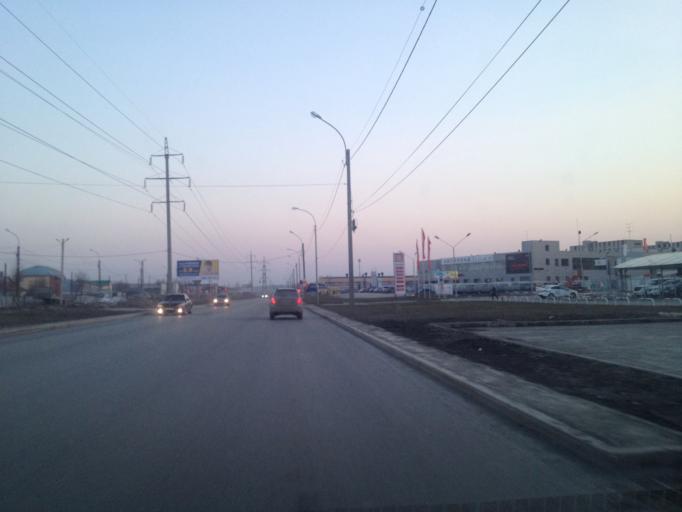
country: RU
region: Sverdlovsk
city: Sovkhoznyy
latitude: 56.7616
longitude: 60.5900
